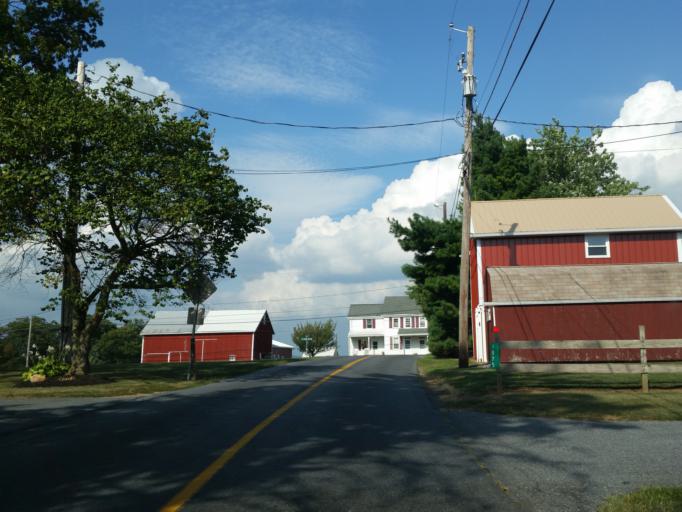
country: US
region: Pennsylvania
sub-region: Lancaster County
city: Manheim
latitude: 40.1714
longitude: -76.4552
